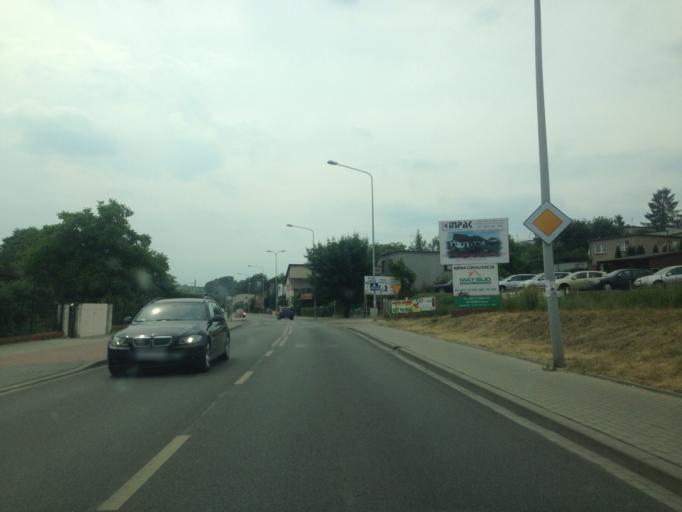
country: PL
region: Kujawsko-Pomorskie
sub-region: Grudziadz
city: Grudziadz
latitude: 53.5032
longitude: 18.7929
